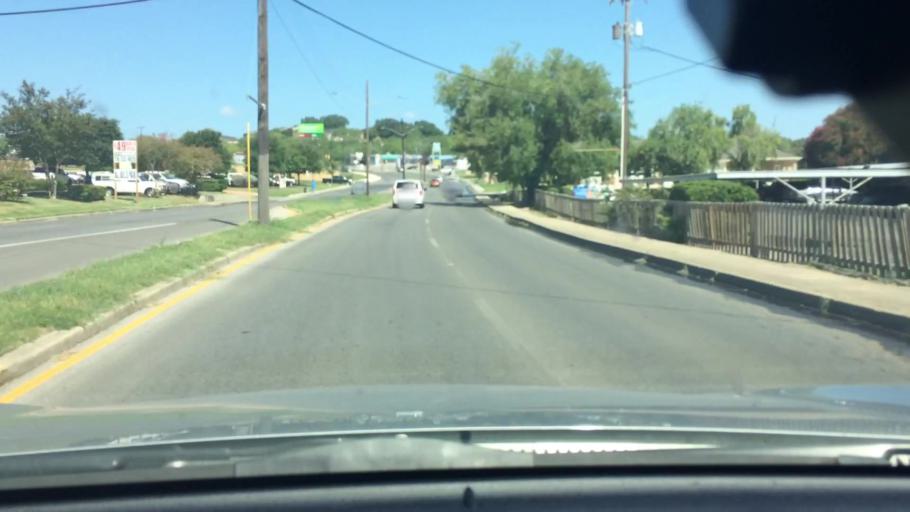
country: US
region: Texas
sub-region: Bexar County
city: San Antonio
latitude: 29.3756
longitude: -98.4299
